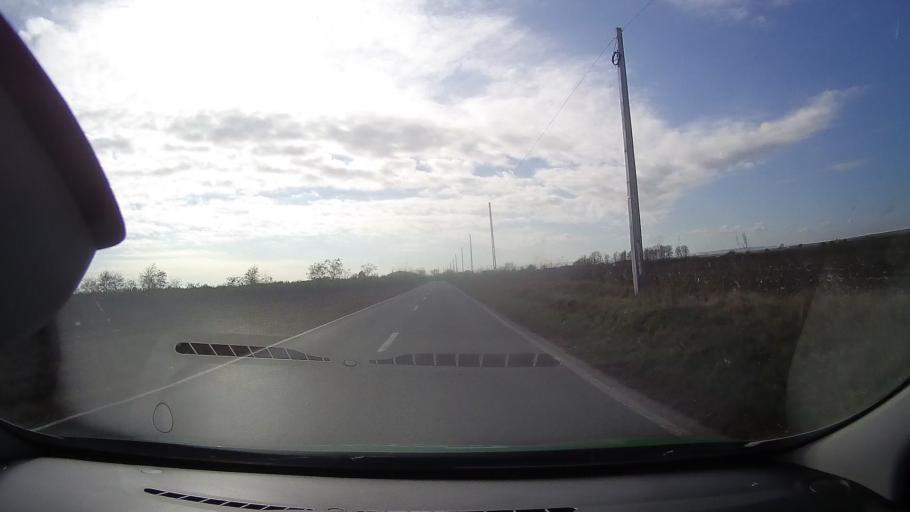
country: RO
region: Tulcea
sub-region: Comuna Sarichioi
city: Sarichioi
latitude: 44.9830
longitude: 28.8836
